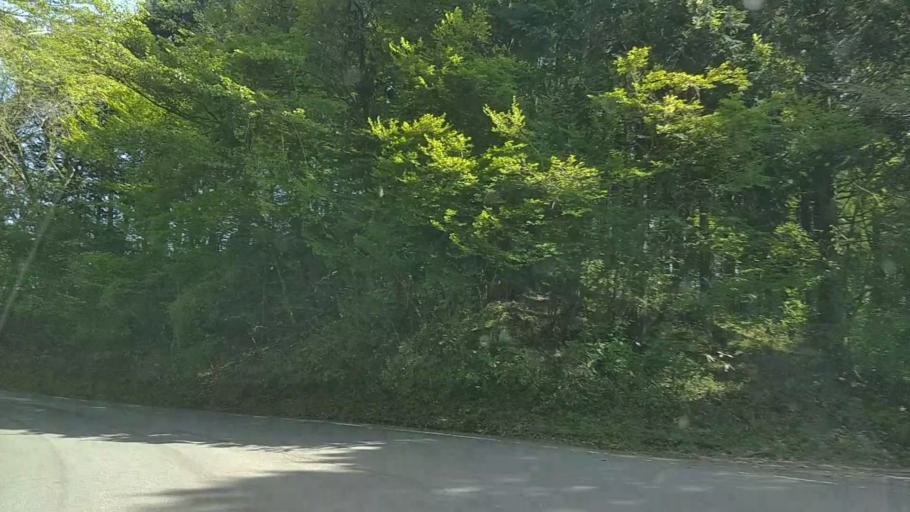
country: JP
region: Shizuoka
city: Gotemba
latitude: 35.2682
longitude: 138.9625
